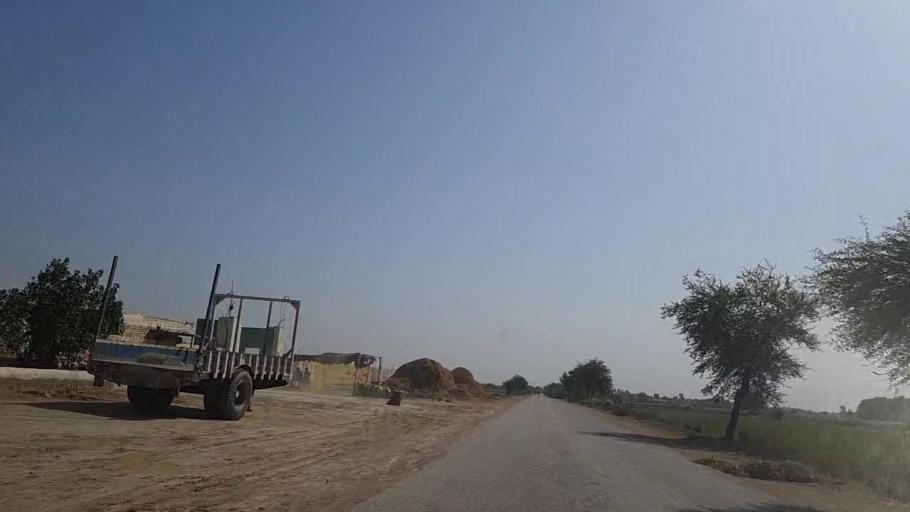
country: PK
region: Sindh
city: Mirpur Batoro
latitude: 24.6123
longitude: 68.2958
